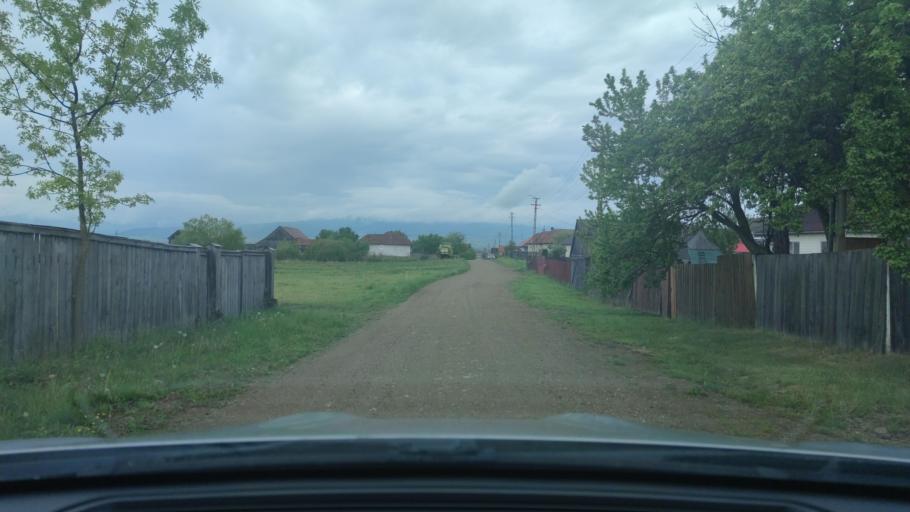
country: RO
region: Harghita
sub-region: Comuna Ditrau
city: Ditrau
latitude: 46.7954
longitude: 25.4946
